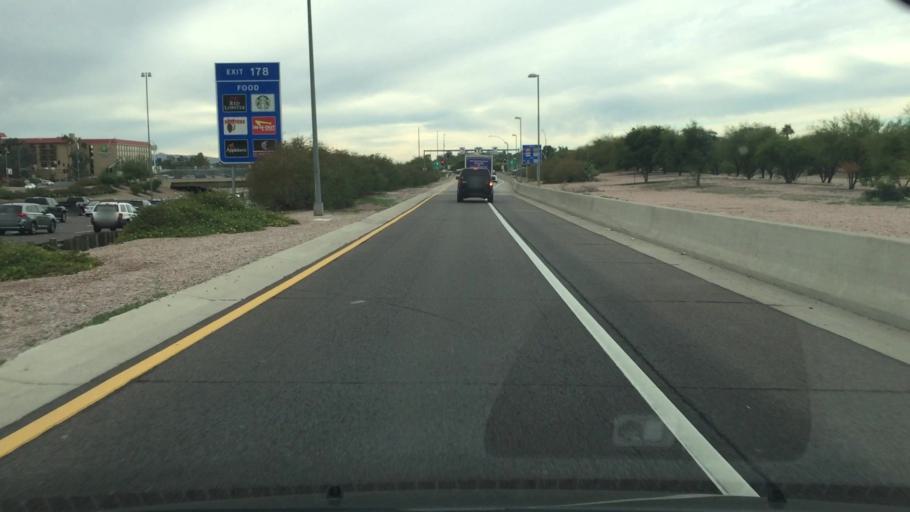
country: US
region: Arizona
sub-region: Maricopa County
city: Mesa
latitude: 33.3864
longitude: -111.8369
